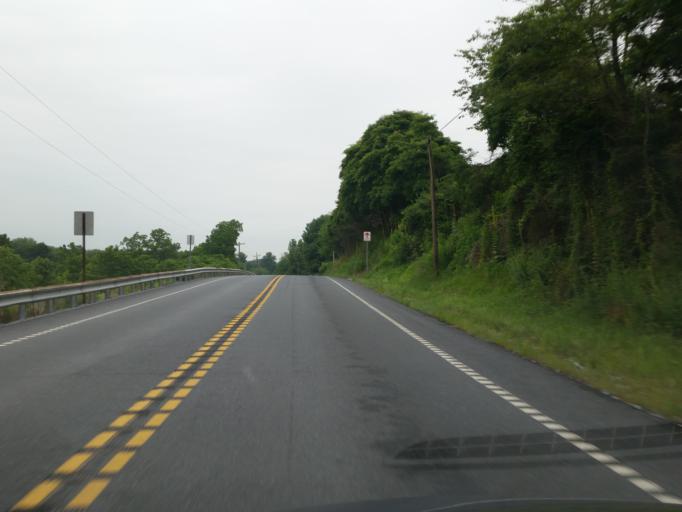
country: US
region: Pennsylvania
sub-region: Schuylkill County
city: Tower City
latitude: 40.5170
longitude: -76.5080
